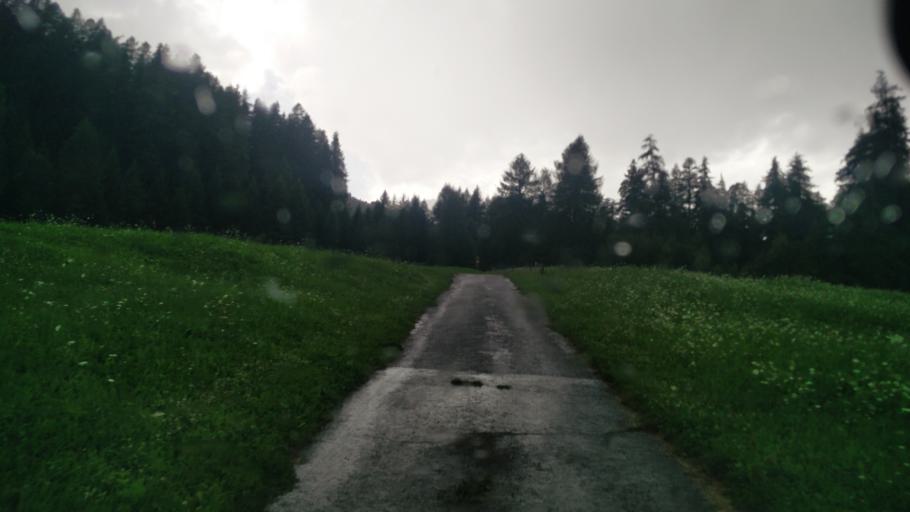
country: IT
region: Trentino-Alto Adige
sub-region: Bolzano
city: Tubre
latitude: 46.6011
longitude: 10.3943
